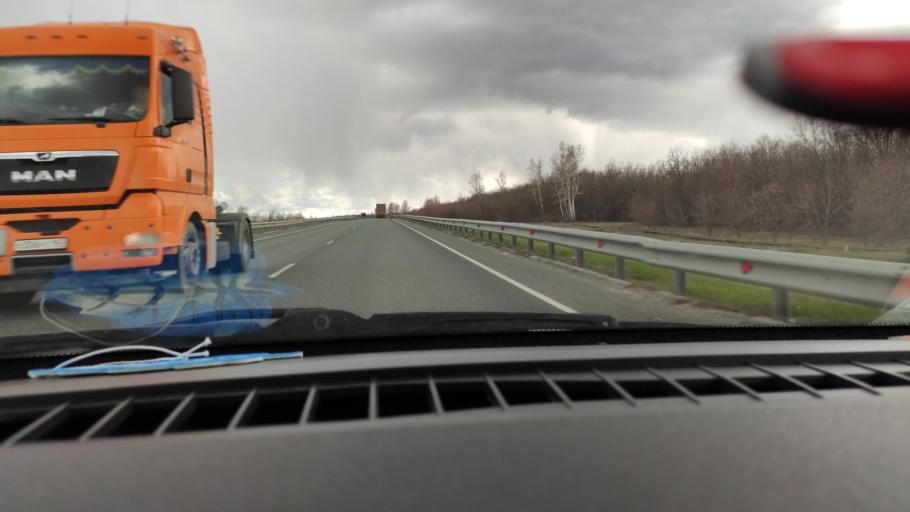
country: RU
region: Saratov
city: Balakovo
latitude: 52.1680
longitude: 47.8275
